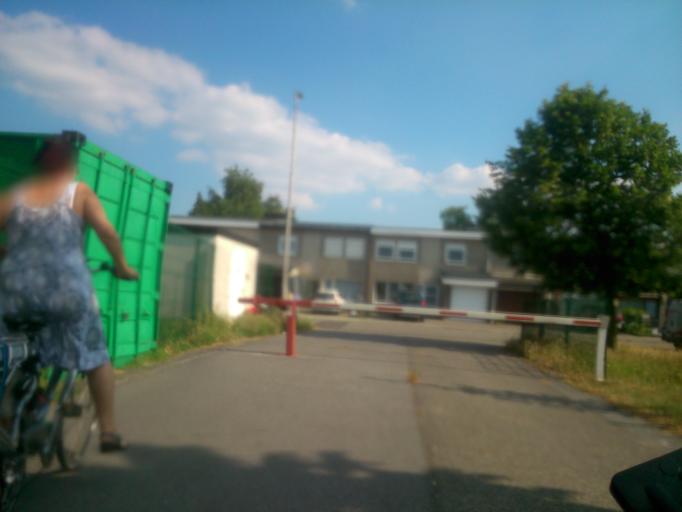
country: BE
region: Flanders
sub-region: Provincie Antwerpen
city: Stabroek
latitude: 51.3470
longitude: 4.3291
